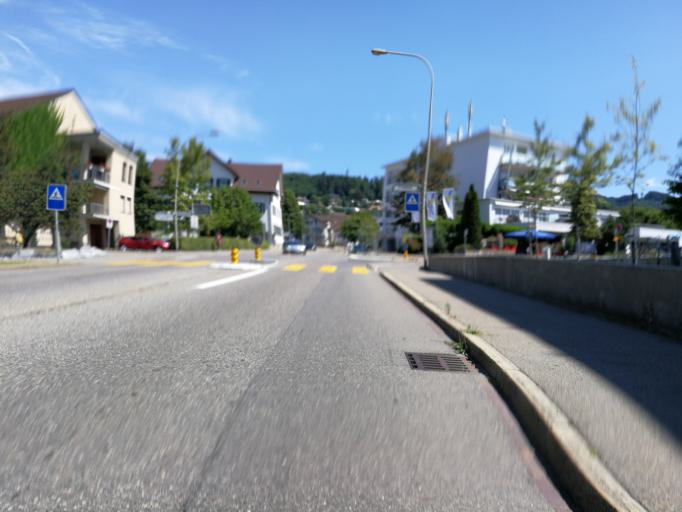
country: CH
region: Zurich
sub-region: Bezirk Hinwil
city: Hinwil
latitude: 47.3006
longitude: 8.8422
